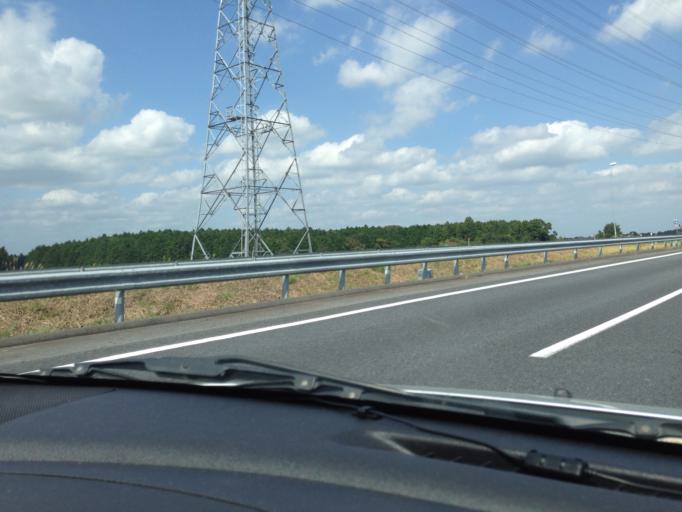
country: JP
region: Ibaraki
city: Tomobe
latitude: 36.3227
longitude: 140.3469
